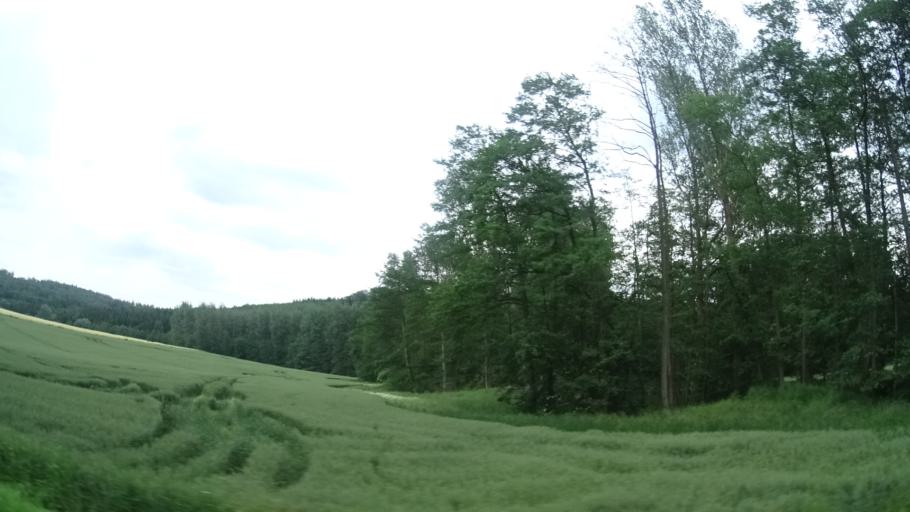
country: DE
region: North Rhine-Westphalia
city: Brakel
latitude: 51.7571
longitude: 9.1773
